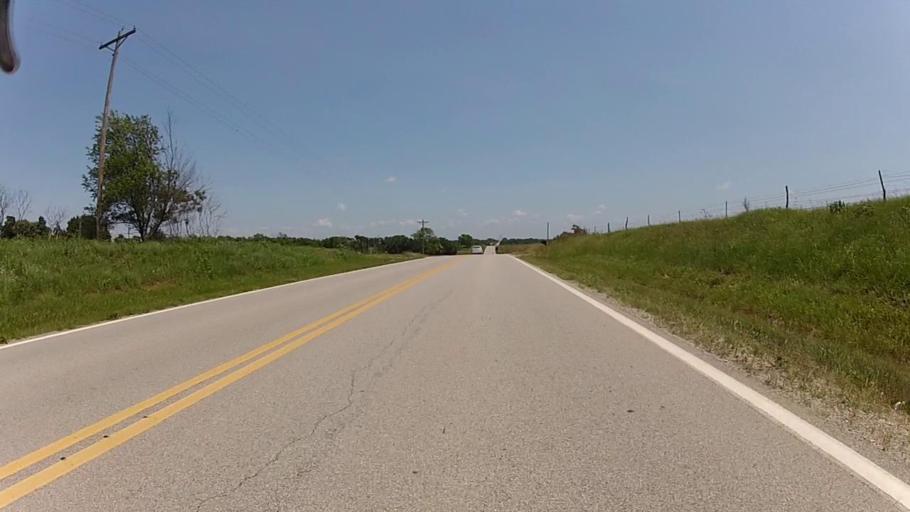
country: US
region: Kansas
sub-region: Montgomery County
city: Cherryvale
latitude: 37.1937
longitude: -95.5243
